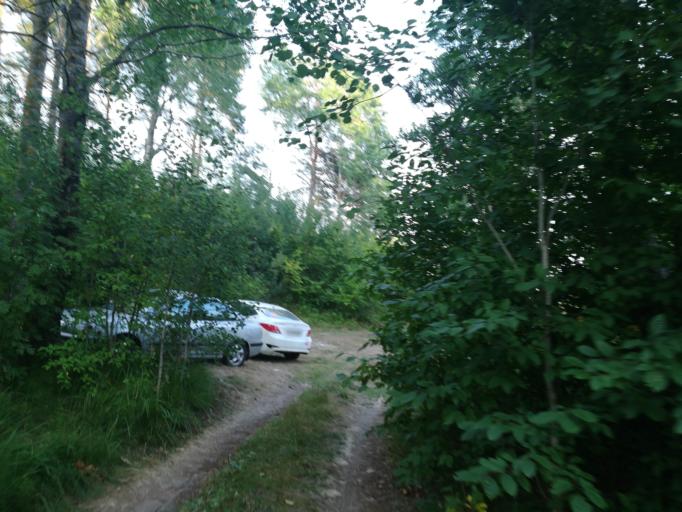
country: RU
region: Leningrad
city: Ust'-Luga
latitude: 59.6773
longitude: 28.2417
